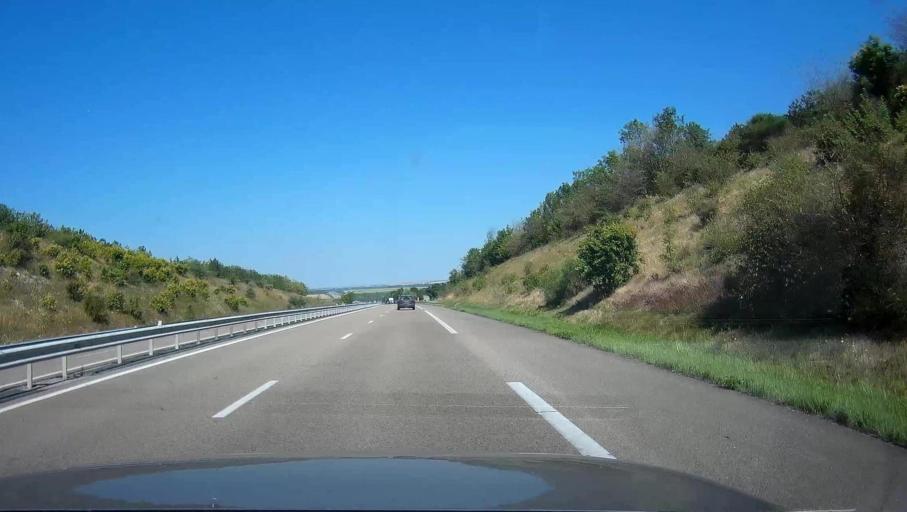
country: FR
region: Champagne-Ardenne
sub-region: Departement de l'Aube
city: Creney-pres-Troyes
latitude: 48.3768
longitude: 4.1574
